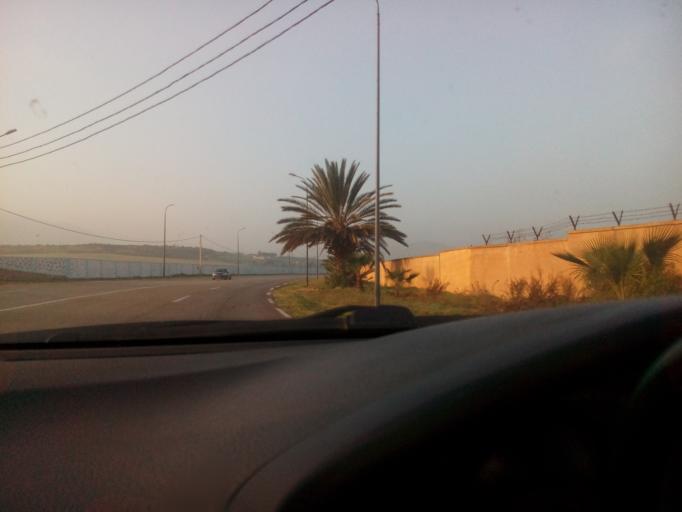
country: DZ
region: Oran
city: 'Ain el Turk
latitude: 35.7135
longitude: -0.8547
